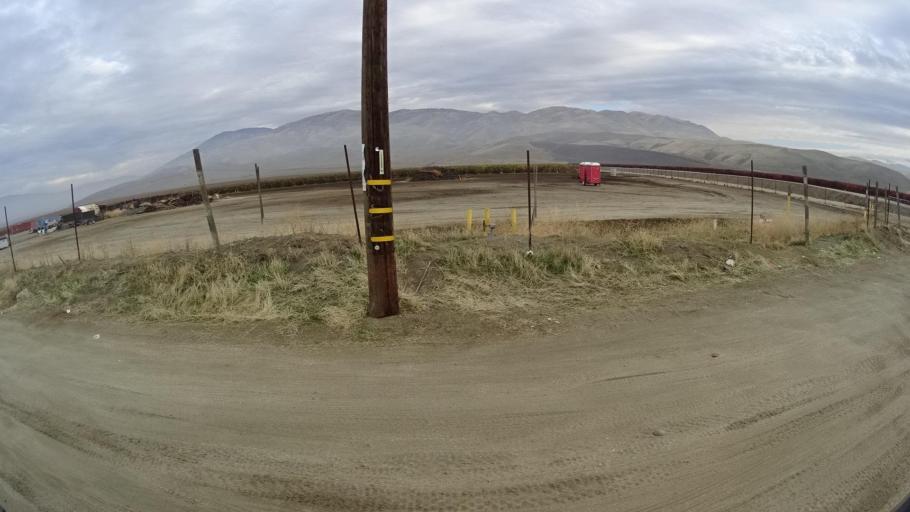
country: US
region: California
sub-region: Kern County
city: Arvin
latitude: 35.1468
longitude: -118.8145
